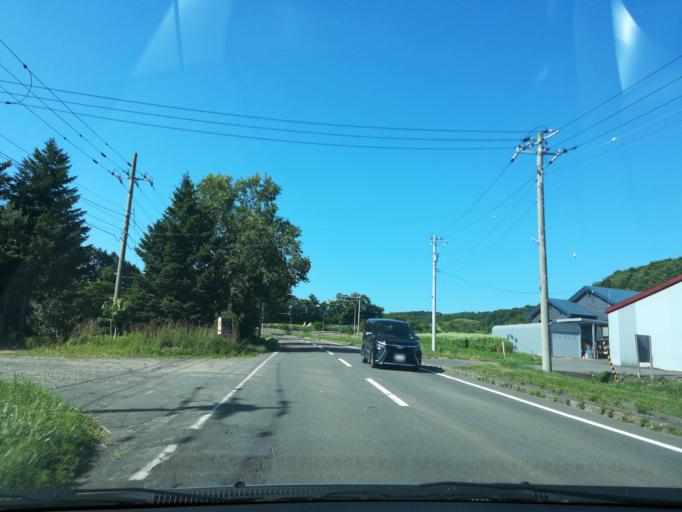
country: JP
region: Hokkaido
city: Chitose
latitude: 42.9139
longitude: 141.7275
